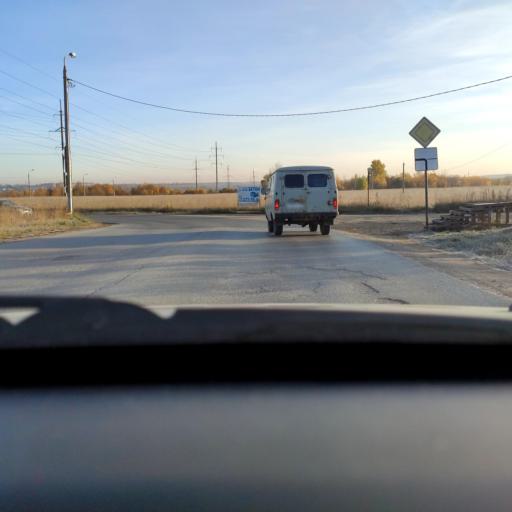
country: RU
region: Perm
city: Perm
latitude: 58.0167
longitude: 56.3351
